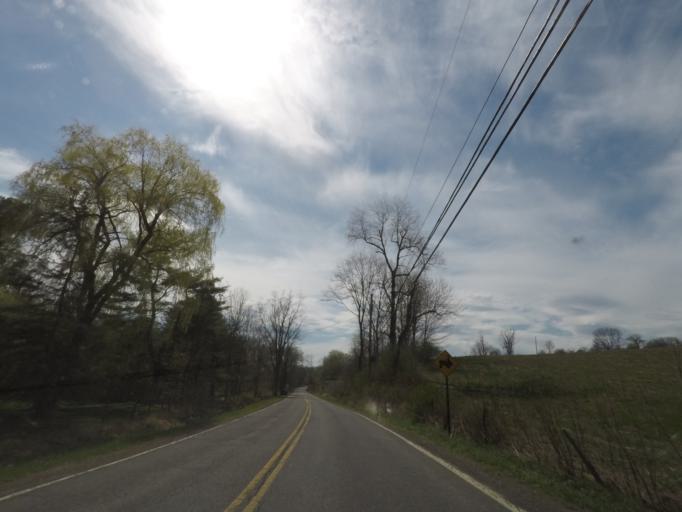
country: US
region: New York
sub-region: Columbia County
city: Chatham
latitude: 42.3561
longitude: -73.5514
